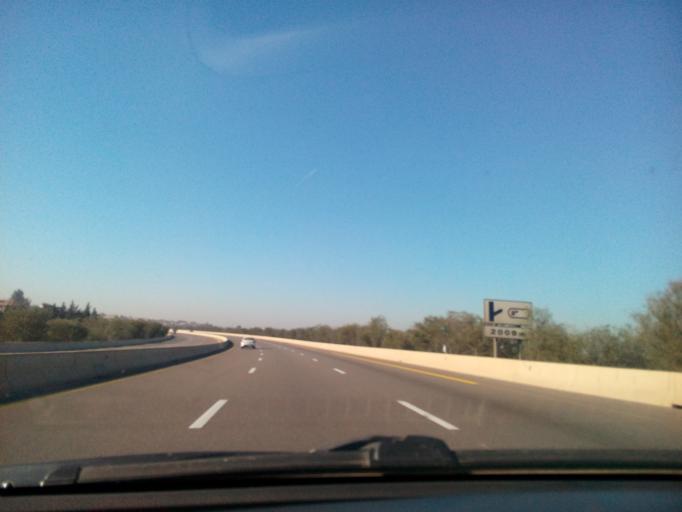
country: DZ
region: Chlef
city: Boukadir
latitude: 36.0671
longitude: 1.1572
